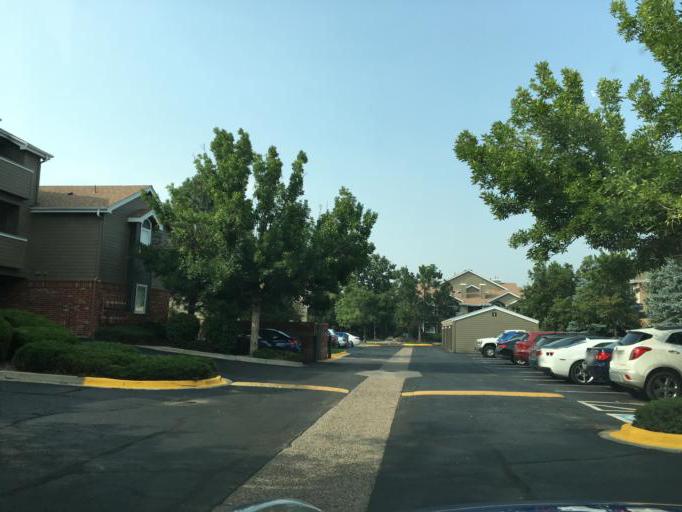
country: US
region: Colorado
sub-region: Arapahoe County
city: Glendale
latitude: 39.7045
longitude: -104.9303
